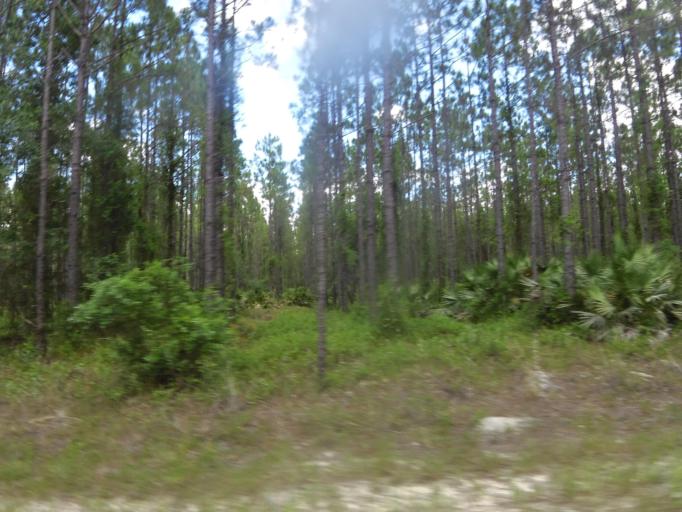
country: US
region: Florida
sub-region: Clay County
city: Keystone Heights
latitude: 29.8591
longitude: -81.8538
